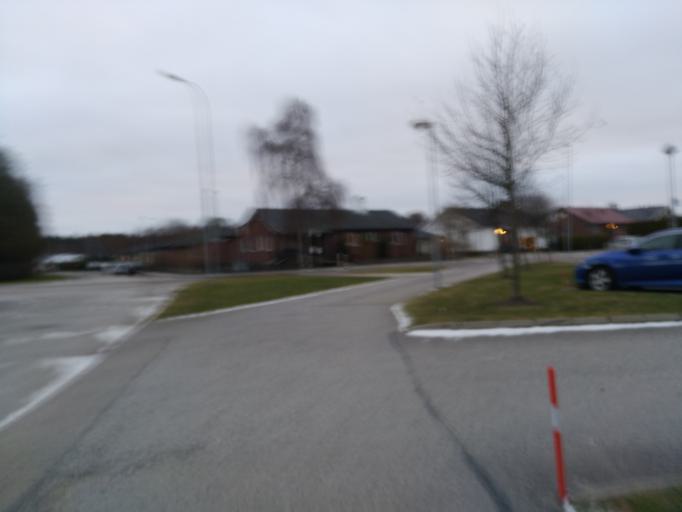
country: SE
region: Vaestra Goetaland
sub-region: Lidkopings Kommun
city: Lidkoping
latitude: 58.4939
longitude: 13.1662
